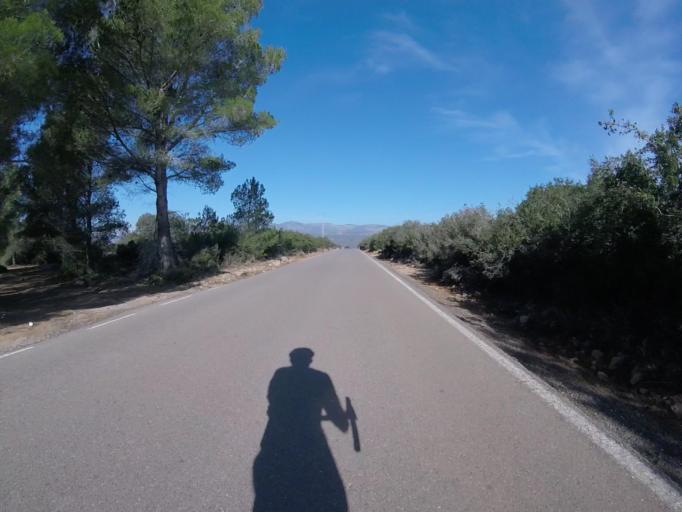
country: ES
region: Valencia
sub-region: Provincia de Castello
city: Benlloch
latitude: 40.2378
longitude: 0.0727
